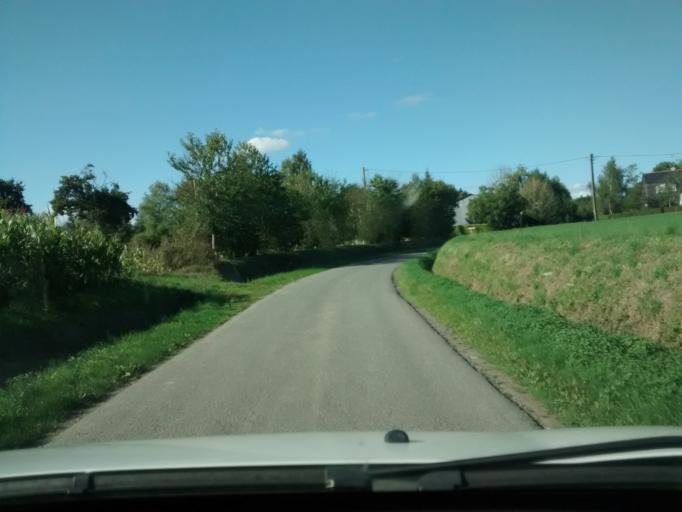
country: FR
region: Brittany
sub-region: Departement d'Ille-et-Vilaine
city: Nouvoitou
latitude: 48.0738
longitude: -1.5638
